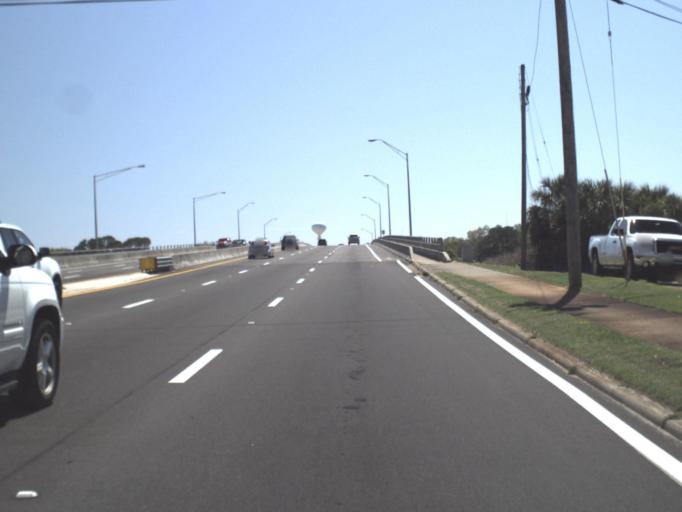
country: US
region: Florida
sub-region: Okaloosa County
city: Ocean City
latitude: 30.4284
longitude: -86.6069
